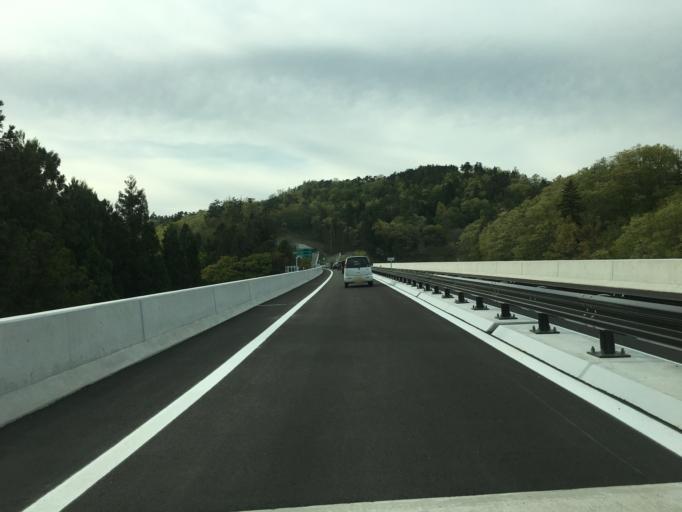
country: JP
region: Fukushima
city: Hobaramachi
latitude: 37.7755
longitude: 140.5825
